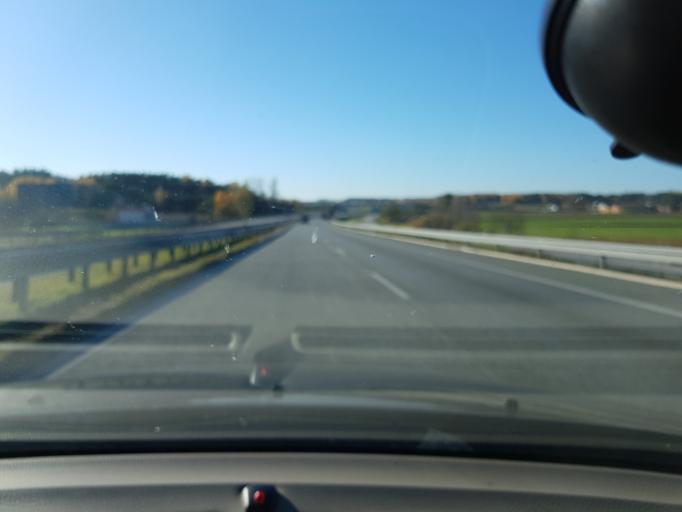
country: PL
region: Lodz Voivodeship
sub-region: Powiat rawski
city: Rawa Mazowiecka
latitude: 51.6987
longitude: 20.2170
